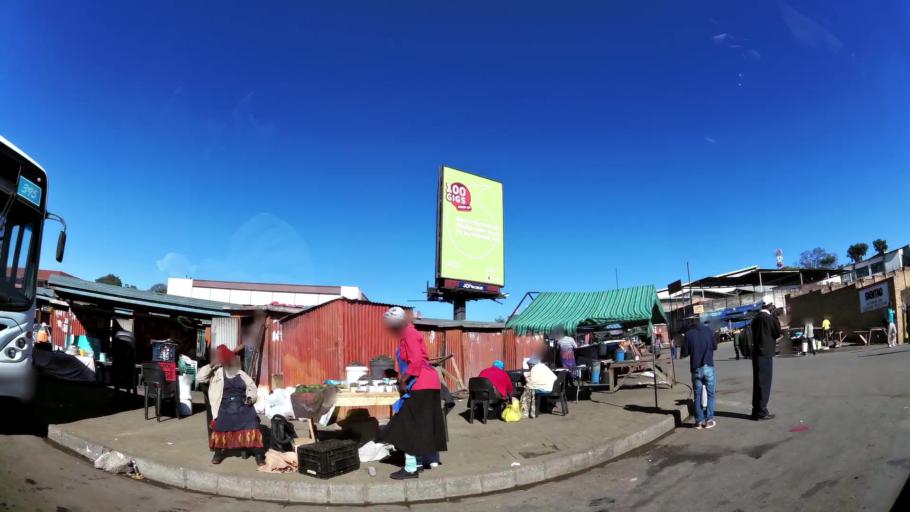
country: ZA
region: Limpopo
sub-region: Mopani District Municipality
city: Tzaneen
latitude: -23.8278
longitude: 30.1643
